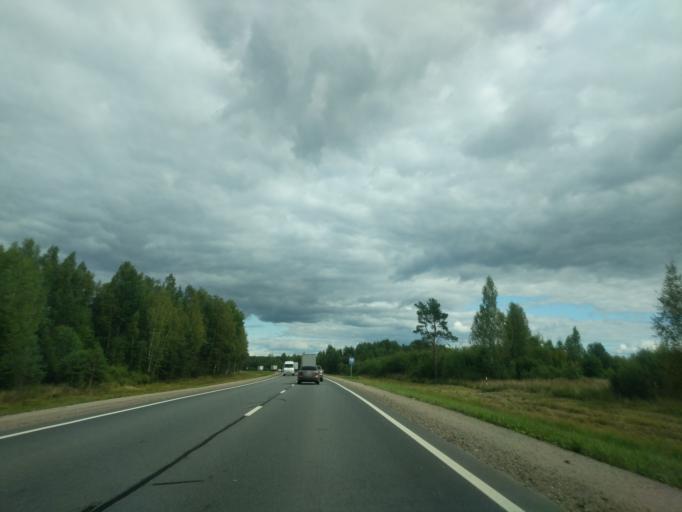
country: RU
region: Kostroma
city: Ostrovskoye
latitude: 57.8146
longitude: 41.9768
